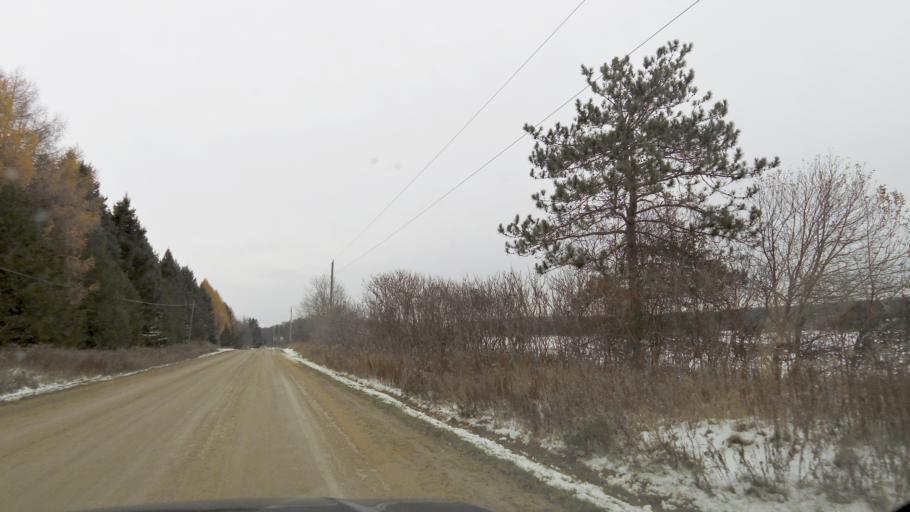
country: CA
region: Ontario
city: Vaughan
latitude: 43.9425
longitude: -79.6107
